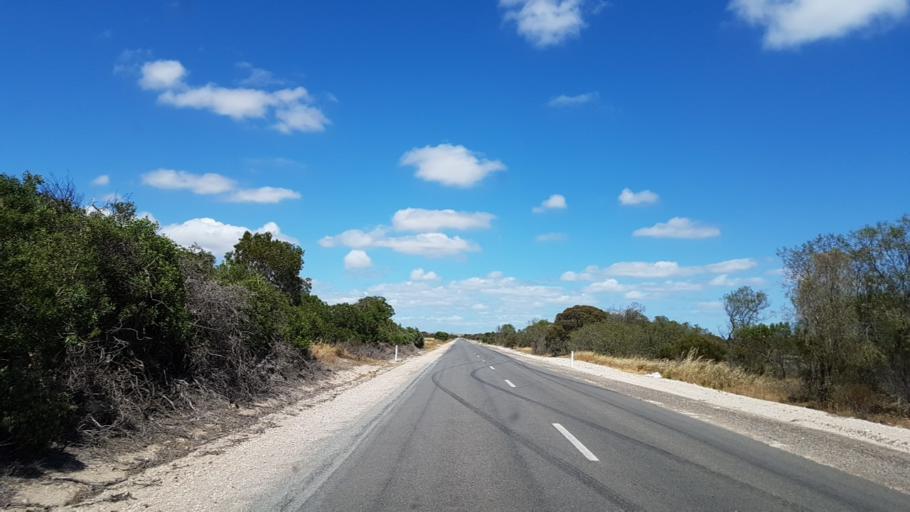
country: AU
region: South Australia
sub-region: Yorke Peninsula
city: Honiton
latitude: -34.9434
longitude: 137.4289
